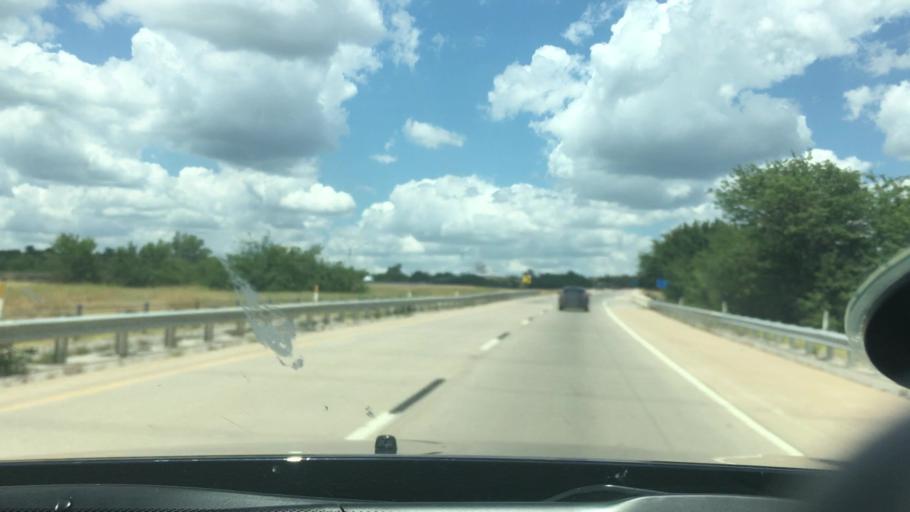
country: US
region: Oklahoma
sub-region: Murray County
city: Davis
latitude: 34.3589
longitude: -97.1483
